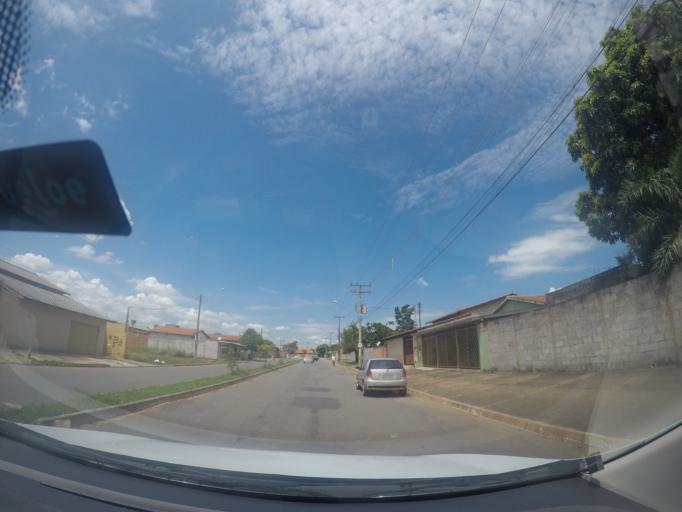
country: BR
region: Goias
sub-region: Goiania
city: Goiania
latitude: -16.6866
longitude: -49.3482
